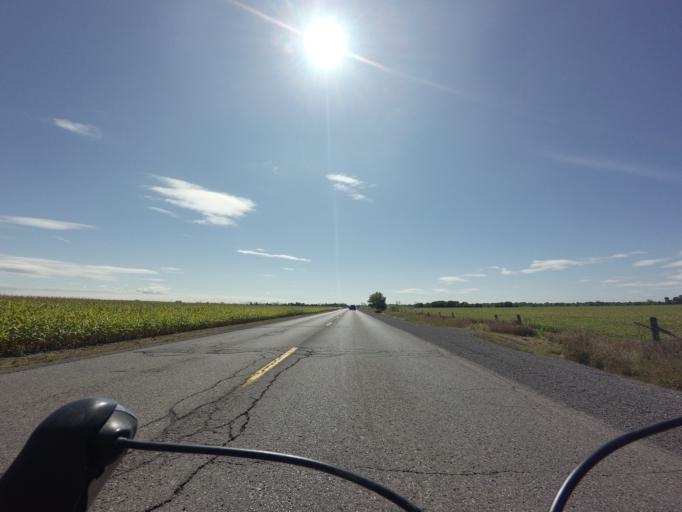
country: CA
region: Ontario
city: Bells Corners
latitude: 45.2213
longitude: -75.8319
